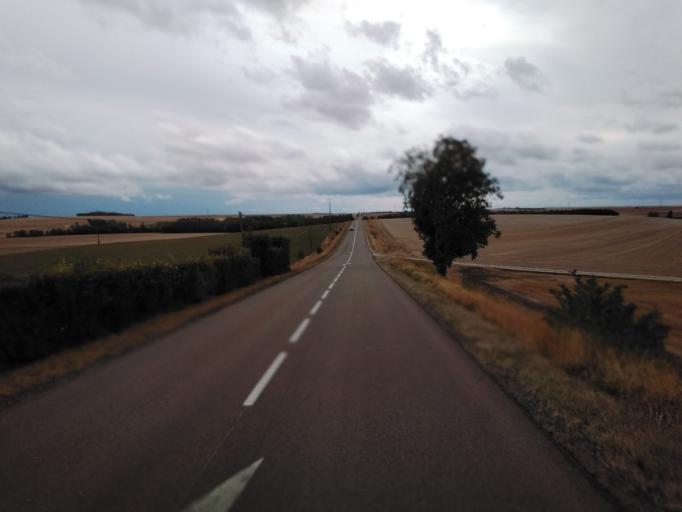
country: FR
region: Champagne-Ardenne
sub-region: Departement de l'Aube
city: Brienne-le-Chateau
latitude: 48.5499
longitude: 4.5221
